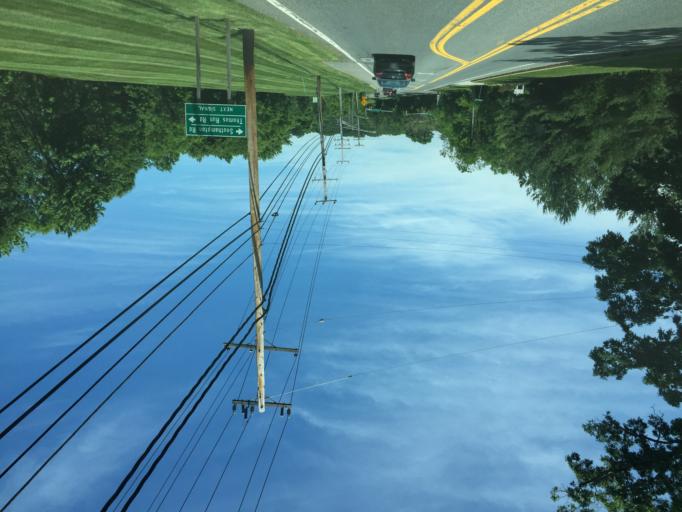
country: US
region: Maryland
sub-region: Harford County
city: South Bel Air
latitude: 39.5544
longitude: -76.3258
